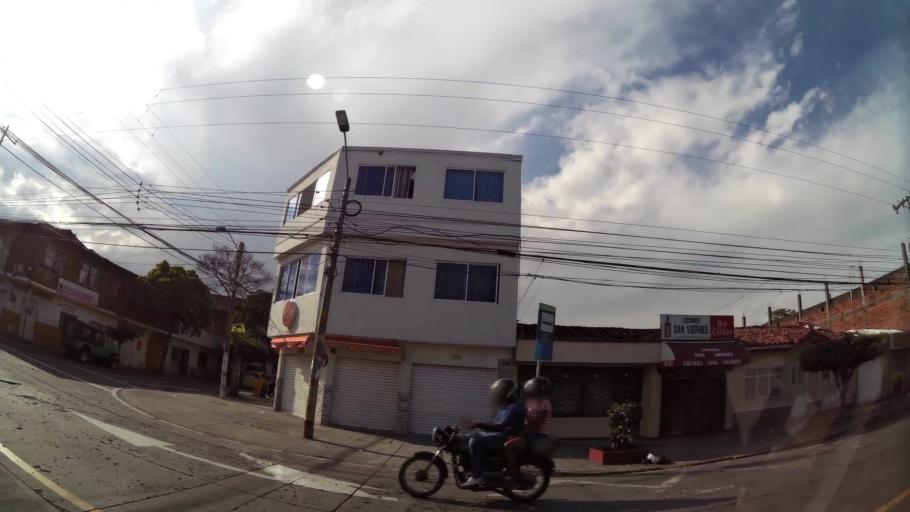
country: CO
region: Valle del Cauca
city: Cali
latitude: 3.4309
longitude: -76.5252
